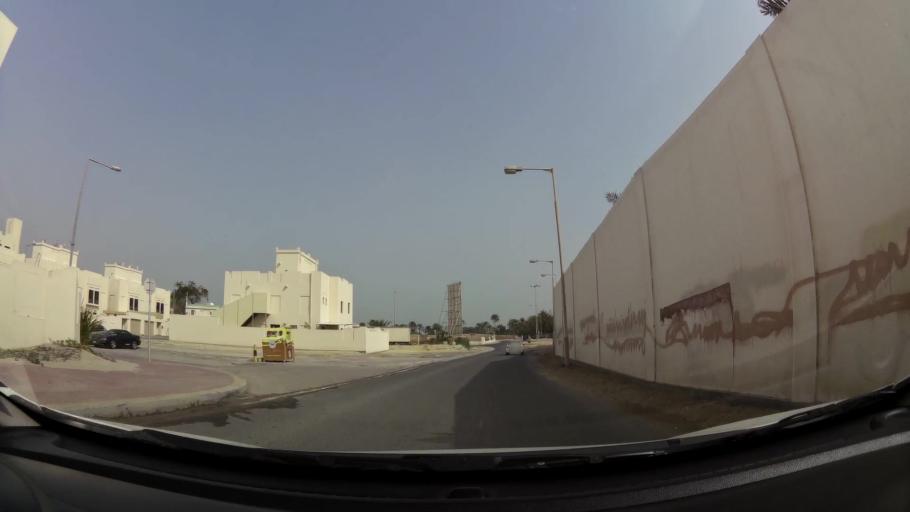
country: BH
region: Manama
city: Jidd Hafs
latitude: 26.2305
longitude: 50.5235
